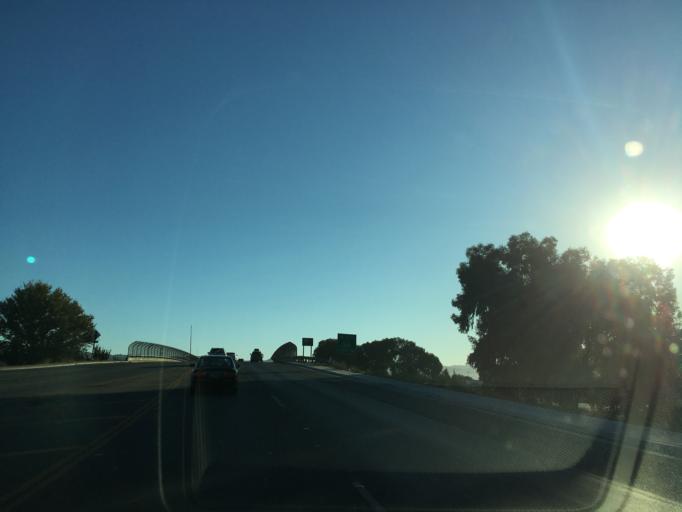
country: US
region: California
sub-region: Santa Clara County
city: Gilroy
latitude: 37.0026
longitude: -121.5578
